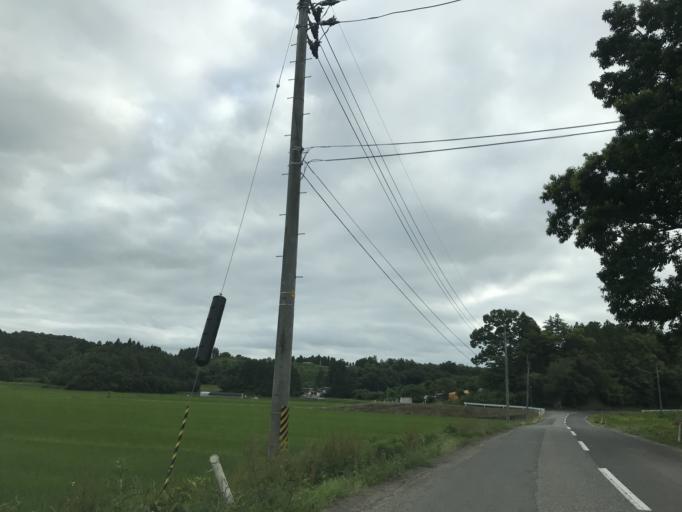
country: JP
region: Iwate
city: Ichinoseki
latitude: 38.7893
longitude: 141.2375
